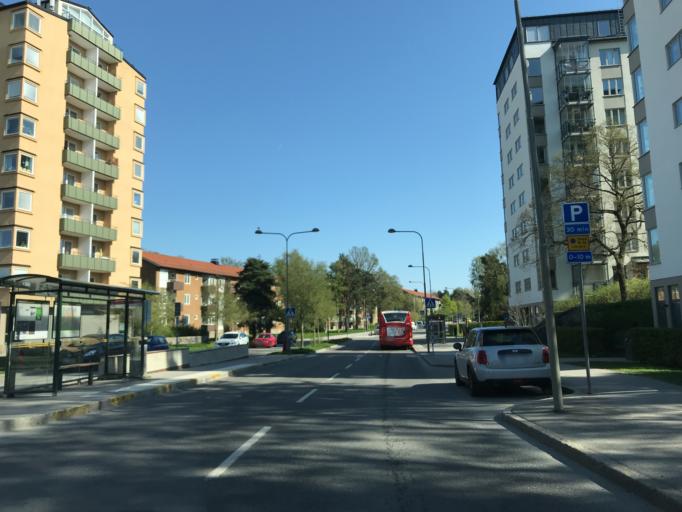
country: SE
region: Stockholm
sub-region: Stockholms Kommun
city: Arsta
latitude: 59.2870
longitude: 18.0089
